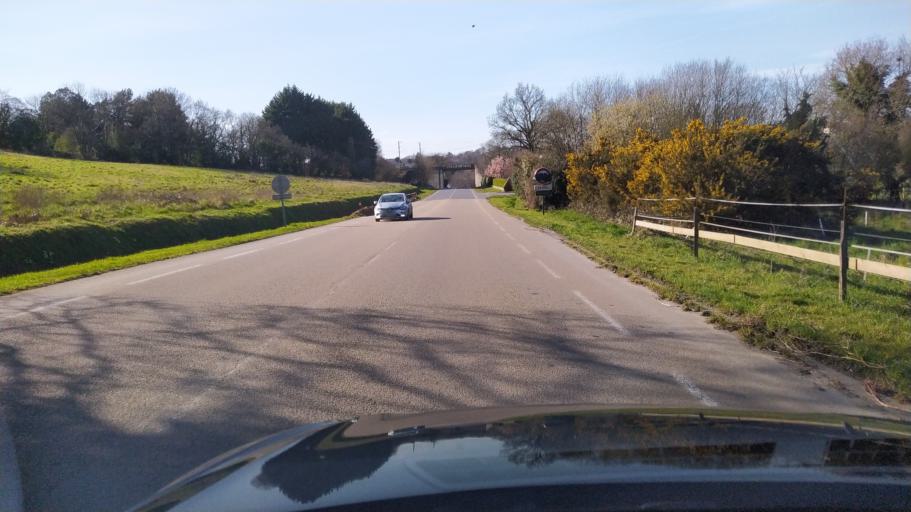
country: FR
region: Brittany
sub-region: Departement du Finistere
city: Lampaul-Guimiliau
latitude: 48.4962
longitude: -4.0522
